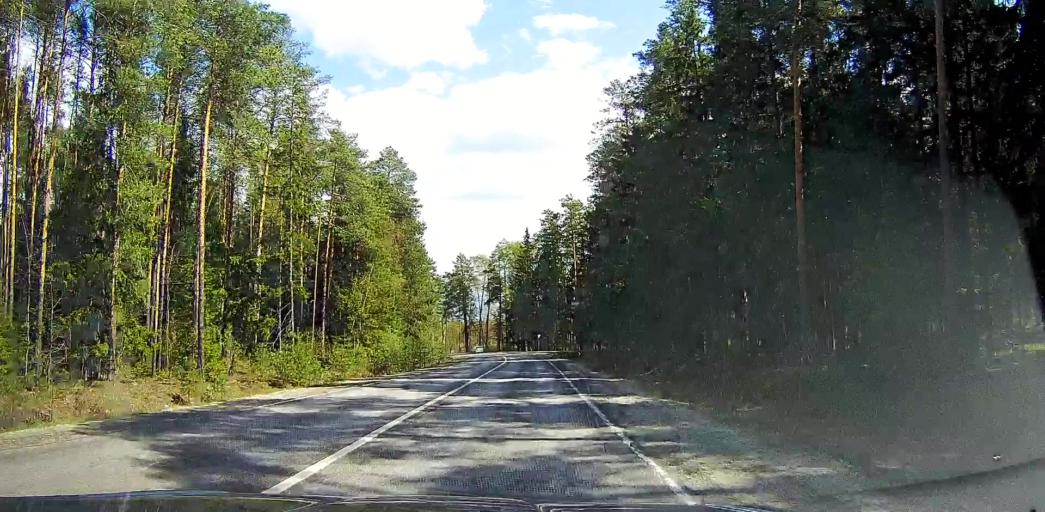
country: RU
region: Moskovskaya
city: Davydovo
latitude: 55.5618
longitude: 38.8489
